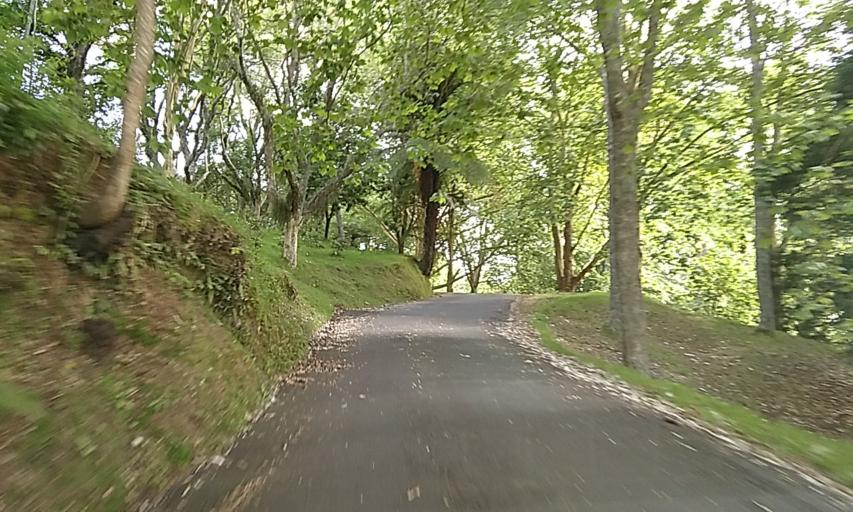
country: NZ
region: Bay of Plenty
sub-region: Tauranga City
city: Tauranga
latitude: -37.8075
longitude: 176.0464
